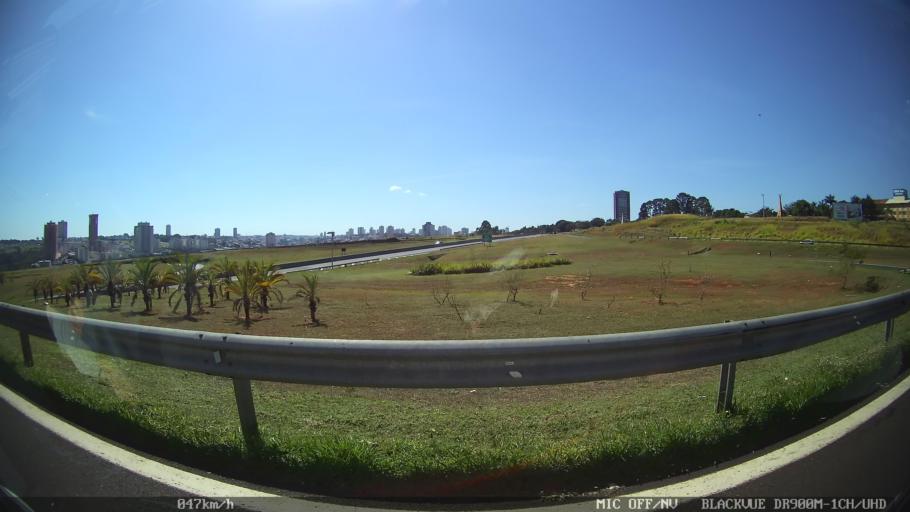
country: BR
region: Sao Paulo
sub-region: Franca
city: Franca
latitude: -20.5624
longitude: -47.4123
